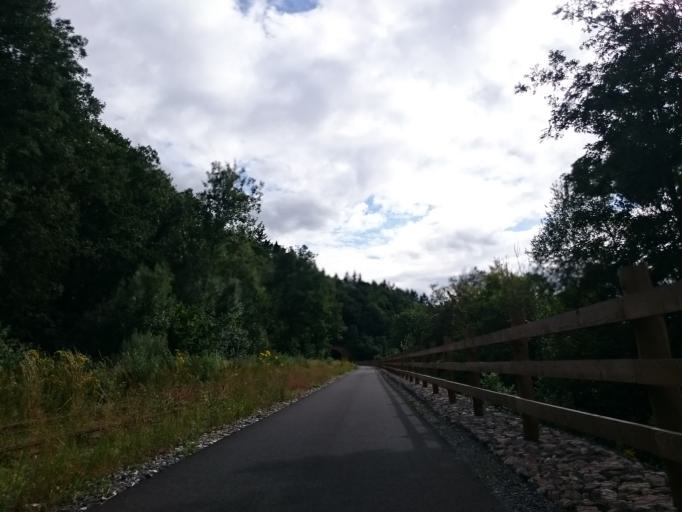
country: FR
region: Lower Normandy
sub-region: Departement du Calvados
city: Thury-Harcourt
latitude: 48.9959
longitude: -0.4806
